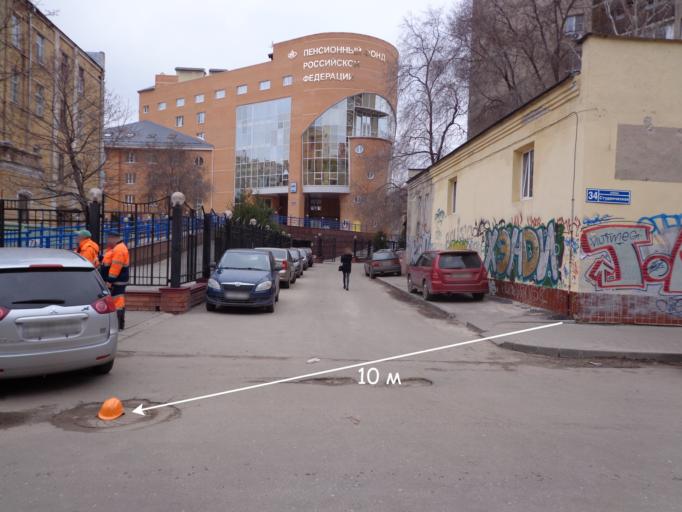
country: RU
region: Voronezj
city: Voronezh
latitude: 51.6705
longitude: 39.2010
